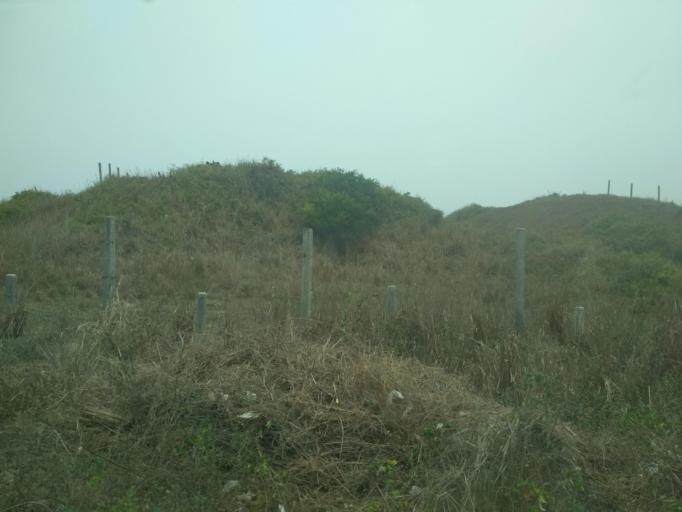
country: MX
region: Veracruz
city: Anton Lizardo
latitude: 19.0540
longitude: -96.0346
